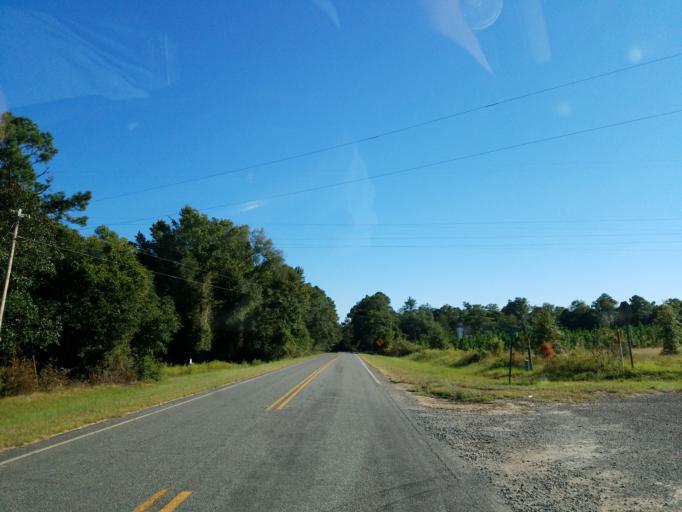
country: US
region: Georgia
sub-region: Dooly County
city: Vienna
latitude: 32.0846
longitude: -83.9601
